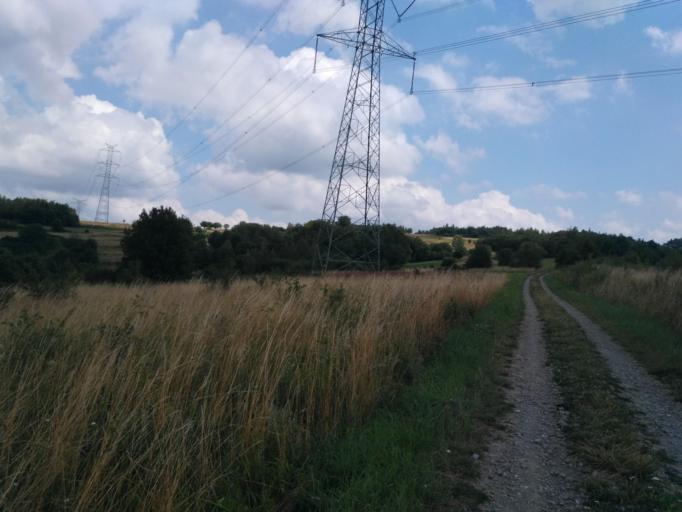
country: PL
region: Subcarpathian Voivodeship
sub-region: Powiat krosnienski
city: Iwonicz-Zdroj
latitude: 49.5737
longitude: 21.7637
